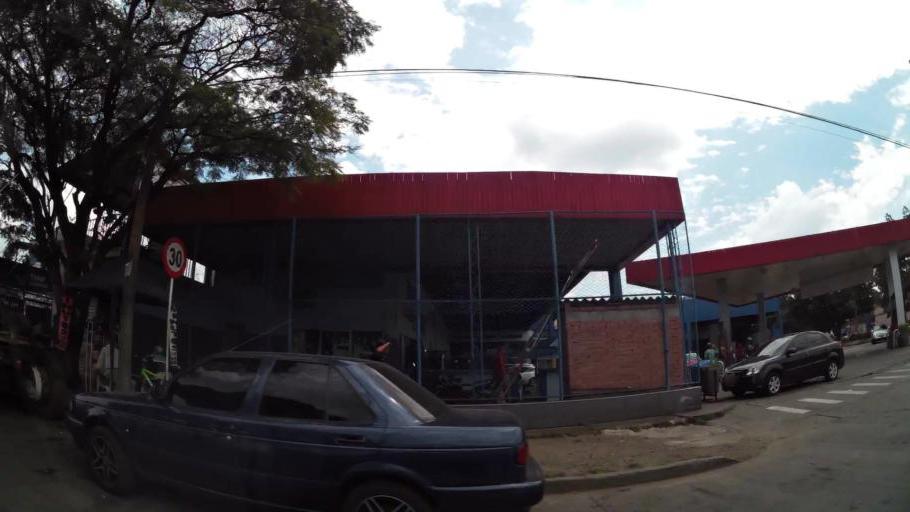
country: CO
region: Valle del Cauca
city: Cali
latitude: 3.4695
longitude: -76.5092
